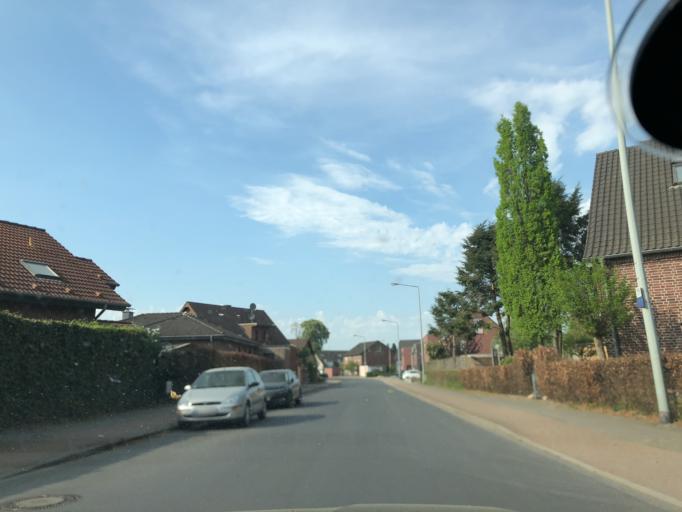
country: DE
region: North Rhine-Westphalia
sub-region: Regierungsbezirk Dusseldorf
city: Wesel
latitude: 51.6571
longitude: 6.6413
